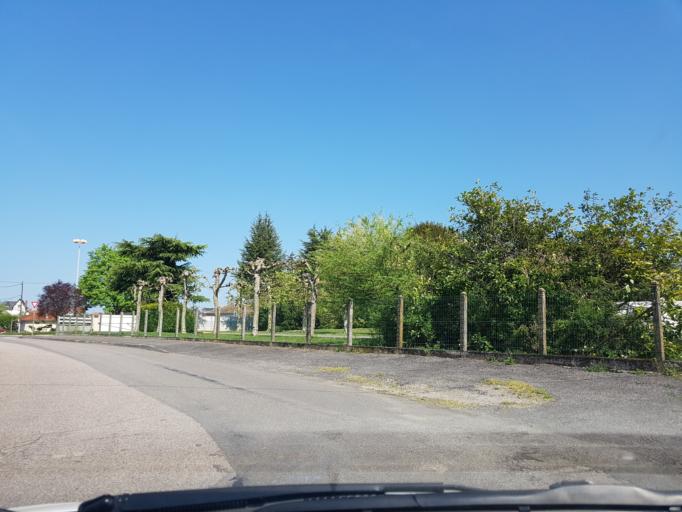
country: FR
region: Limousin
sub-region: Departement de la Haute-Vienne
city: Saint-Junien
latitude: 45.8928
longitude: 0.9139
